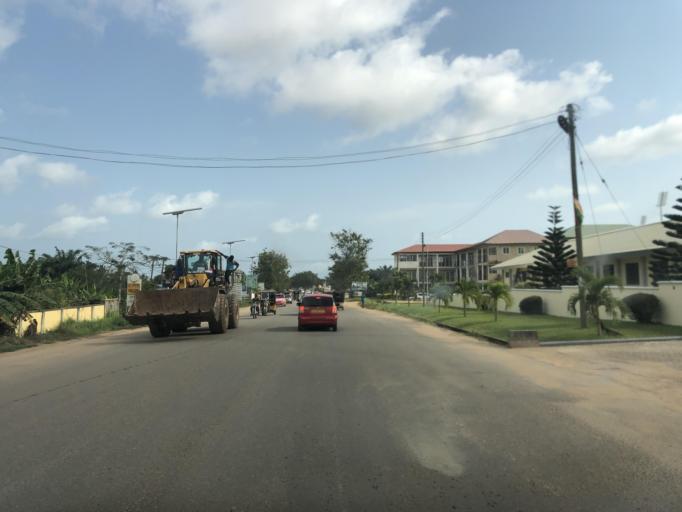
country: GH
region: Central
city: Cape Coast
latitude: 5.1407
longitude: -1.2823
